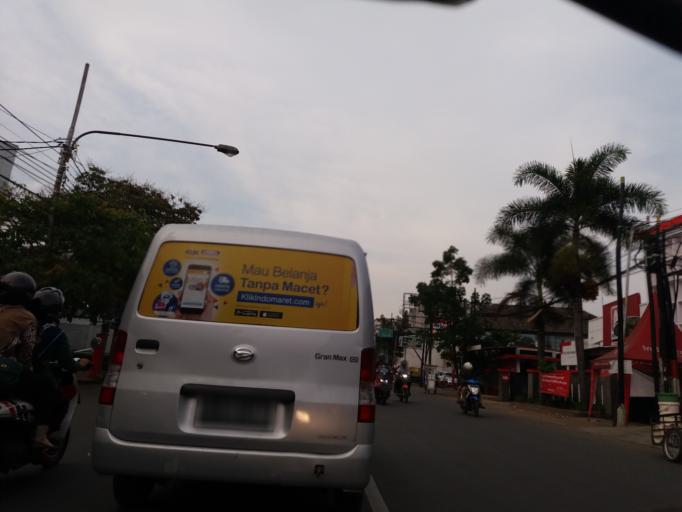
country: ID
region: West Java
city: Bandung
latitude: -6.9055
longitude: 107.6494
